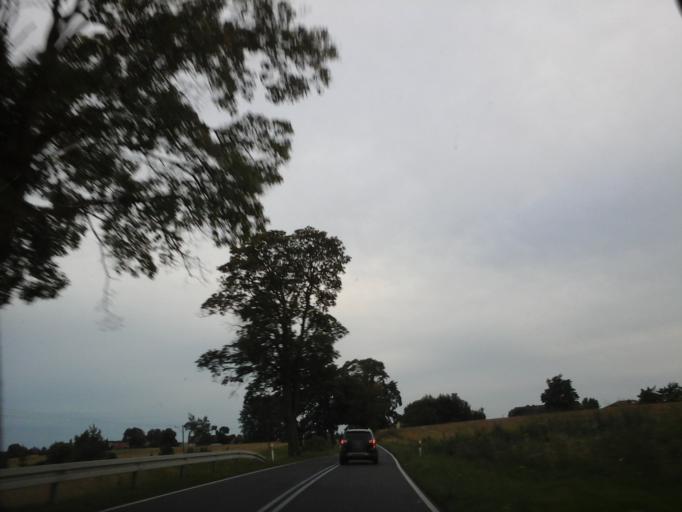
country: PL
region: West Pomeranian Voivodeship
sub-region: Powiat stargardzki
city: Stargard Szczecinski
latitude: 53.3913
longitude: 15.0854
